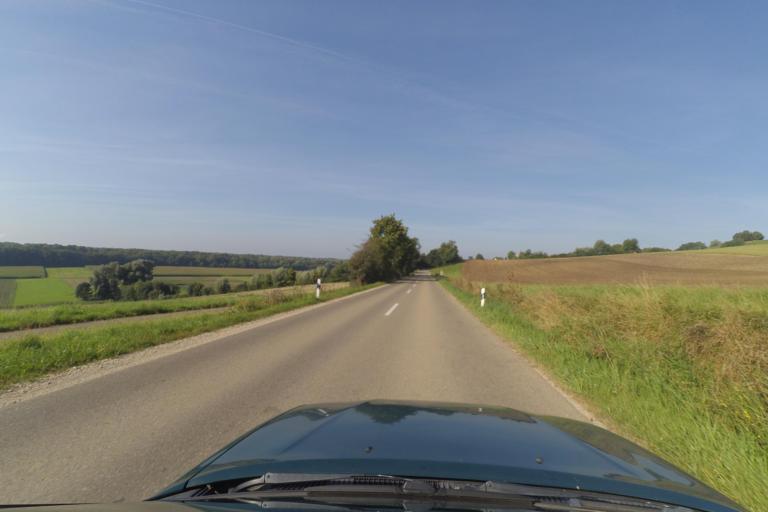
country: DE
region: Bavaria
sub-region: Swabia
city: Marxheim
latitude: 48.7420
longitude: 10.9231
